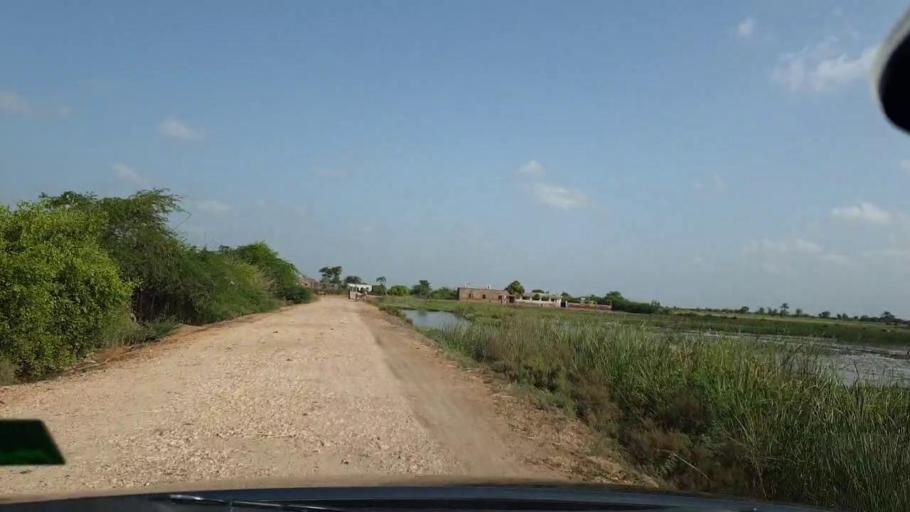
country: PK
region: Sindh
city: Tando Bago
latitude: 24.6459
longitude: 69.0940
